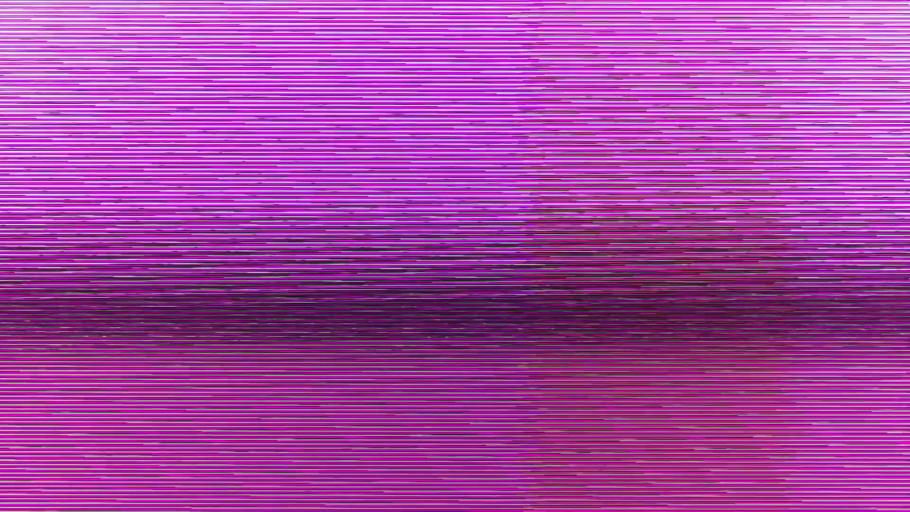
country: US
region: Michigan
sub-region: Wayne County
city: Canton
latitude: 42.3235
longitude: -83.4881
